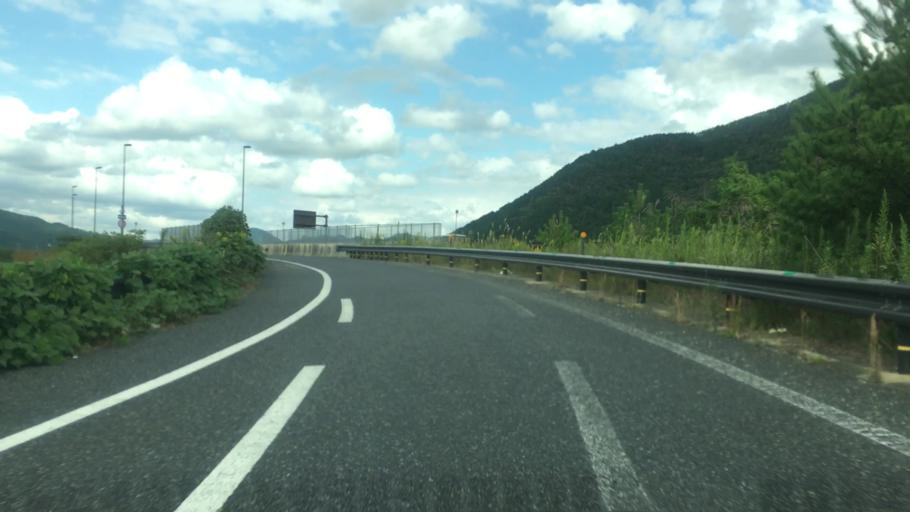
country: JP
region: Kyoto
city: Fukuchiyama
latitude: 35.1638
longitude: 135.0448
